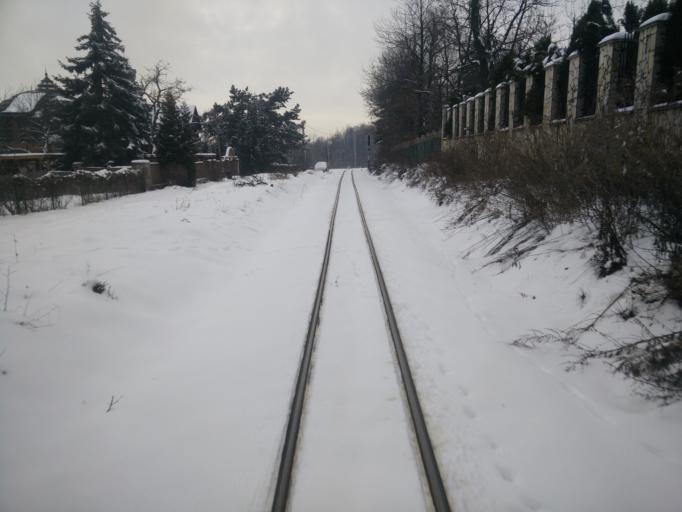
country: HU
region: Pest
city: Budaors
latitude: 47.4992
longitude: 18.9647
